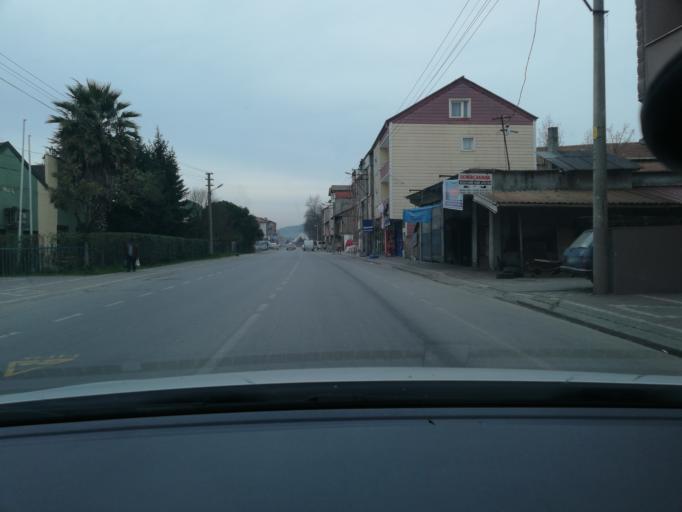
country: TR
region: Zonguldak
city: Caycuma
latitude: 41.4200
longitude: 32.0944
